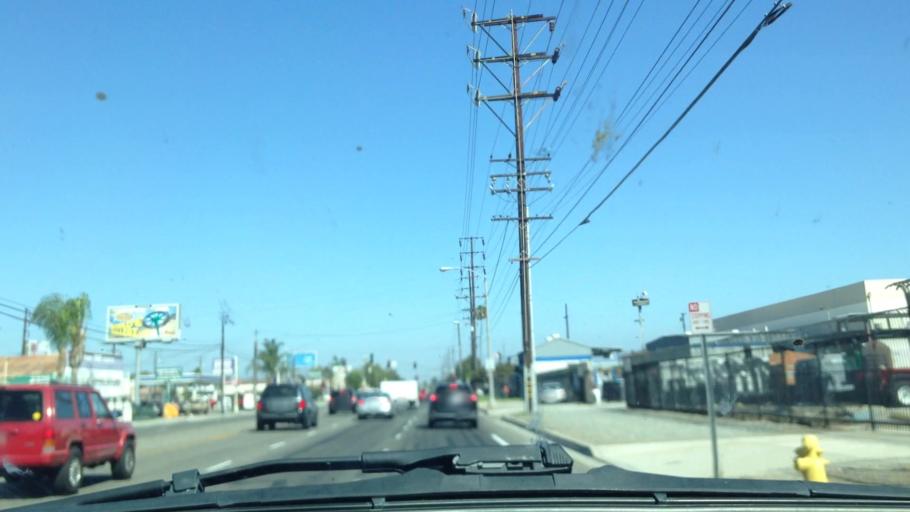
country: US
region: California
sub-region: Orange County
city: Placentia
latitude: 33.8596
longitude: -117.8914
